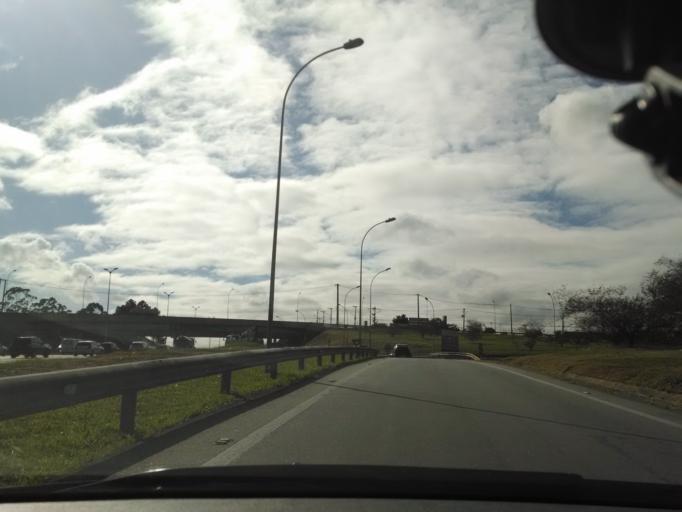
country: BR
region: Sao Paulo
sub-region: Taboao Da Serra
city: Taboao da Serra
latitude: -23.5928
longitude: -46.8091
